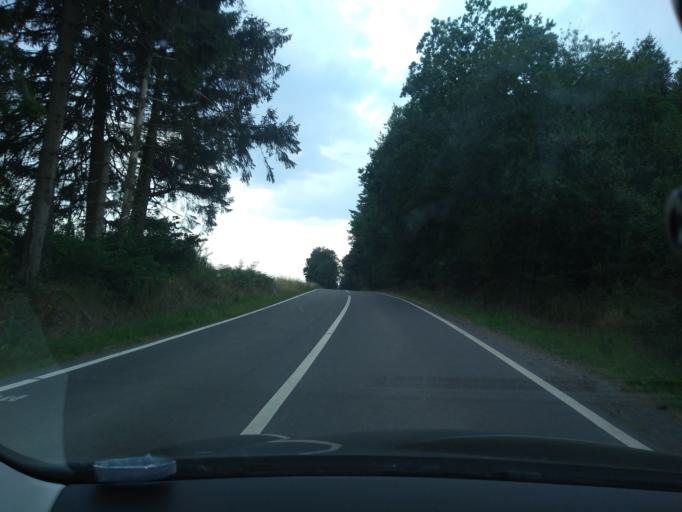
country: BE
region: Wallonia
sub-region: Province du Luxembourg
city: Tenneville
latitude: 50.0512
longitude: 5.5758
